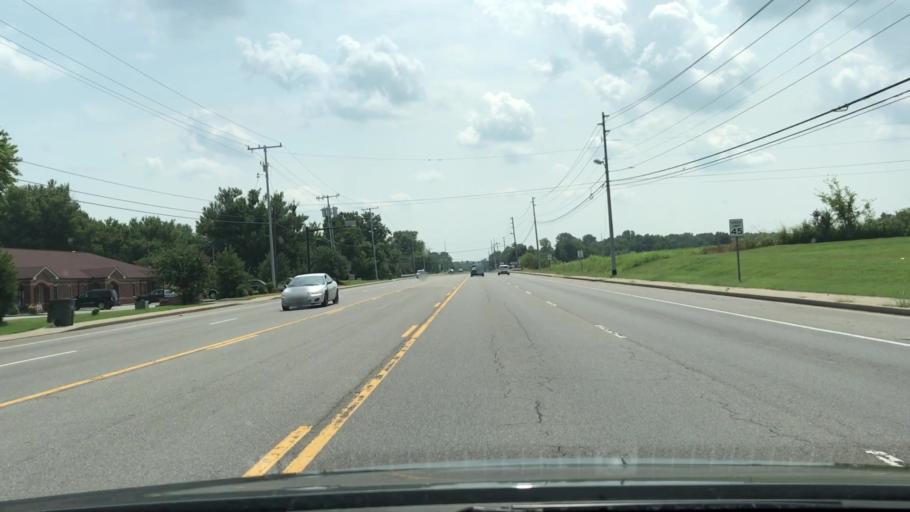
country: US
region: Tennessee
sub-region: Sumner County
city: Portland
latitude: 36.5542
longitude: -86.5077
